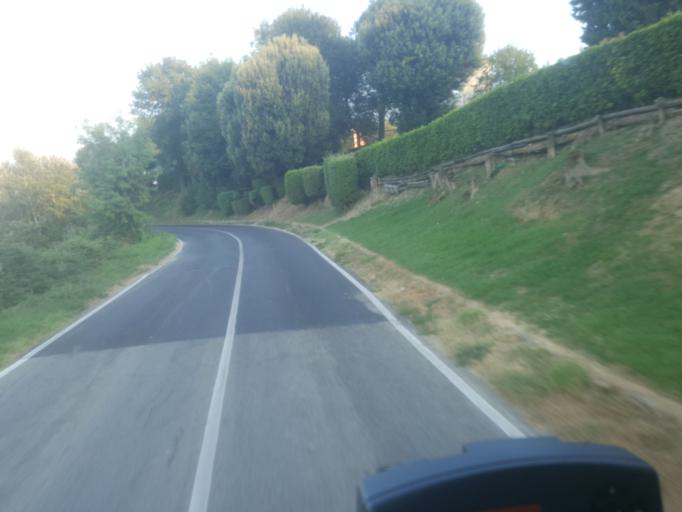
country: IT
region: Tuscany
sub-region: Province of Florence
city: Gambassi Terme
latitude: 43.5450
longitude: 10.9739
